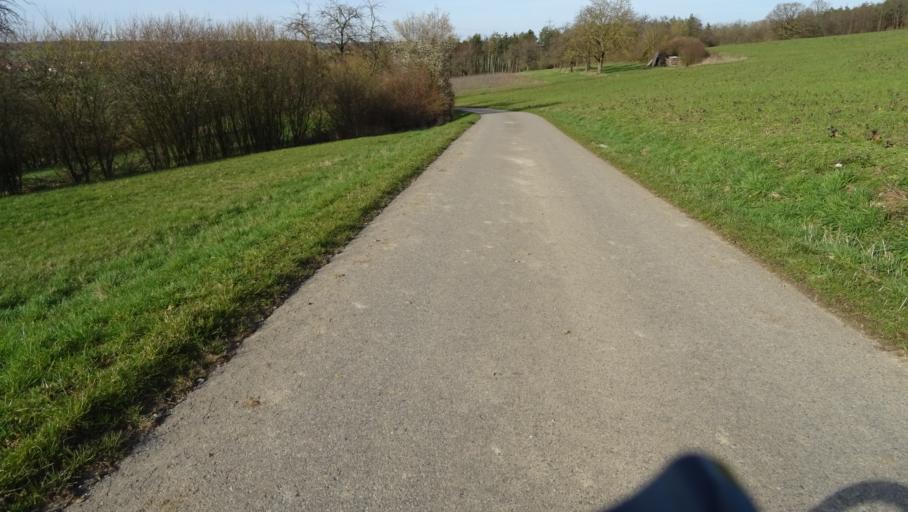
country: DE
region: Baden-Wuerttemberg
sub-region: Karlsruhe Region
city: Seckach
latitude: 49.4164
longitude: 9.2936
